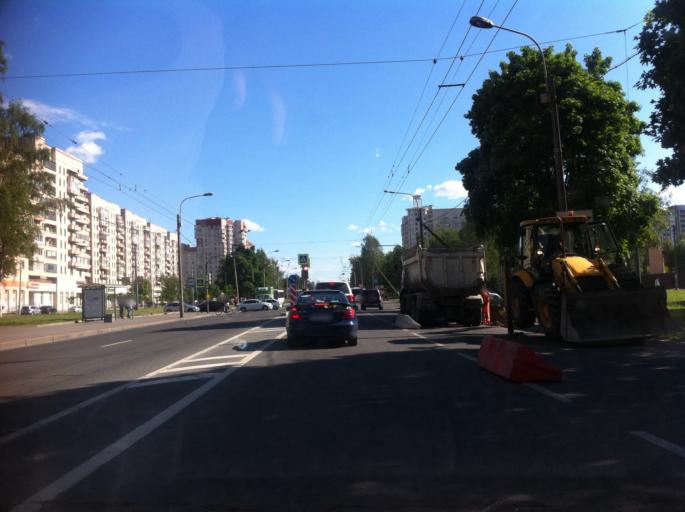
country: RU
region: St.-Petersburg
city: Uritsk
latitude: 59.8366
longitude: 30.1755
